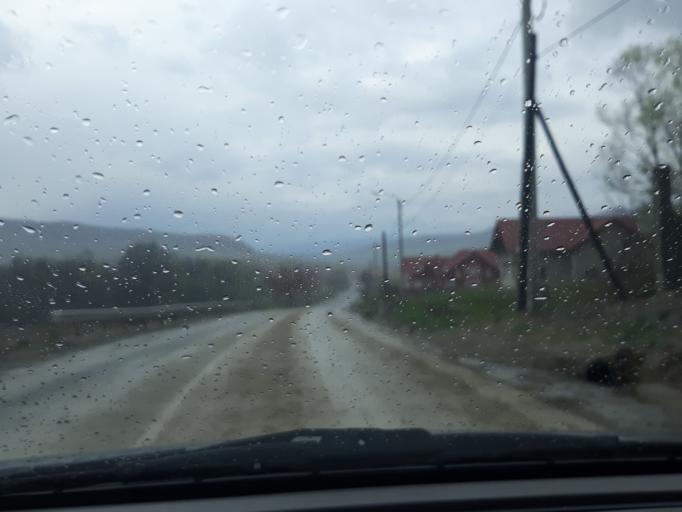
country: RO
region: Harghita
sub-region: Comuna Corund
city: Corund
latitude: 46.4804
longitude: 25.1728
